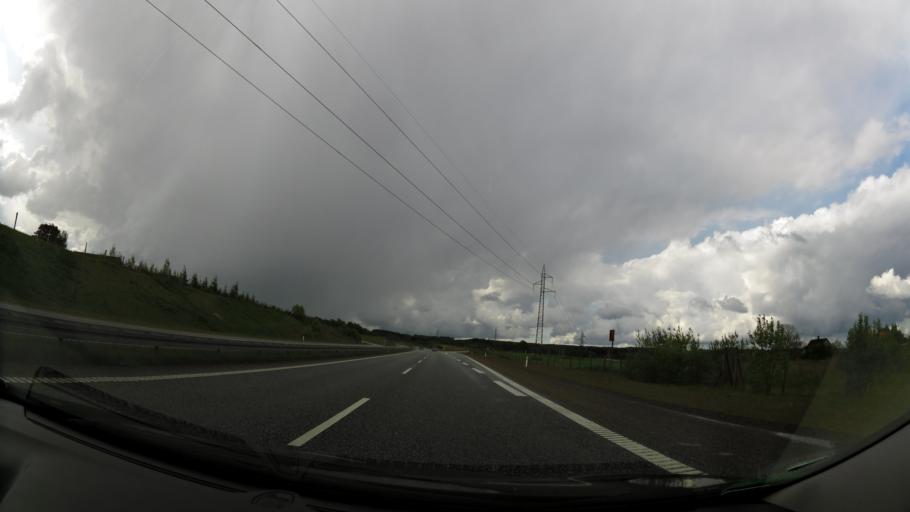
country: DK
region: South Denmark
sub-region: Svendborg Kommune
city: Svendborg
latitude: 55.1187
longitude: 10.5603
